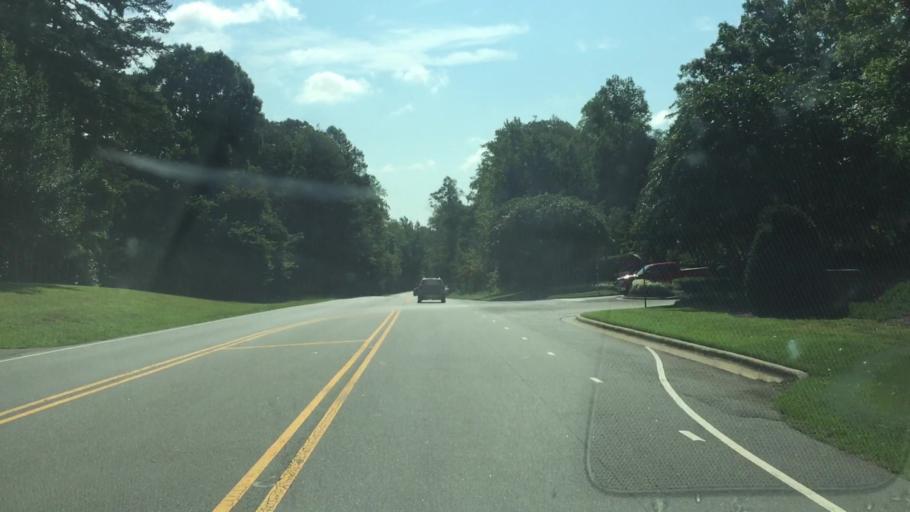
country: US
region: North Carolina
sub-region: Mecklenburg County
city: Mint Hill
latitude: 35.1719
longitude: -80.6099
